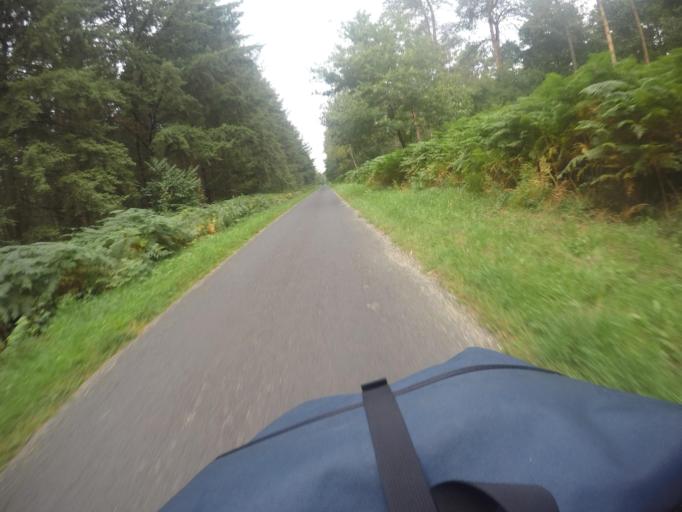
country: DE
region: North Rhine-Westphalia
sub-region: Regierungsbezirk Dusseldorf
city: Kranenburg
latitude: 51.7352
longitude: 6.0197
